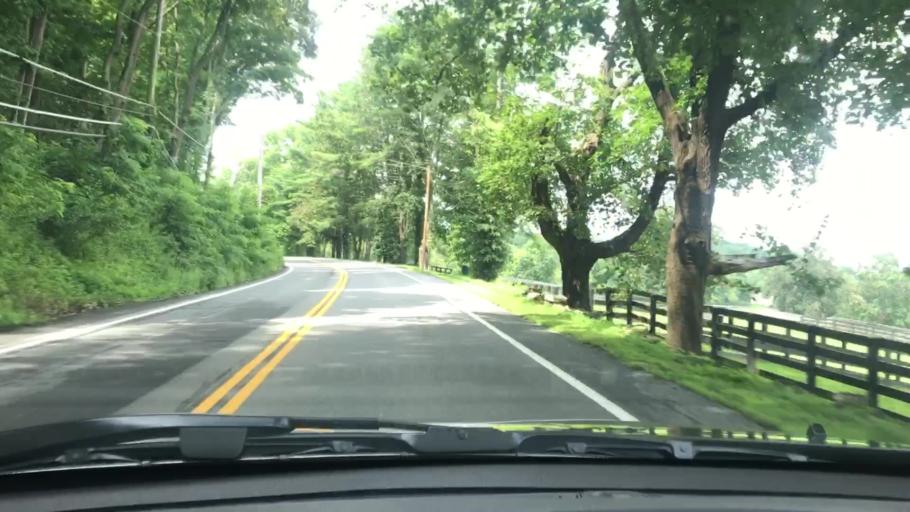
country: US
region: New York
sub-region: Westchester County
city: Bedford
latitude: 41.1971
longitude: -73.6637
